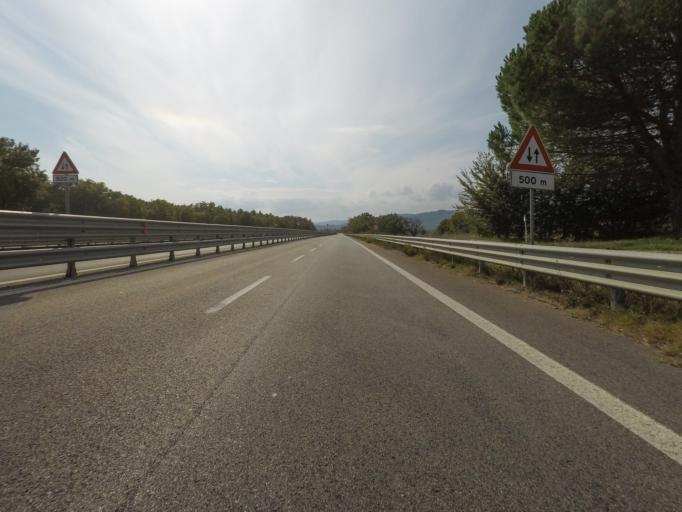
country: IT
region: Tuscany
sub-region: Provincia di Siena
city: Rosia
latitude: 43.2285
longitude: 11.2754
